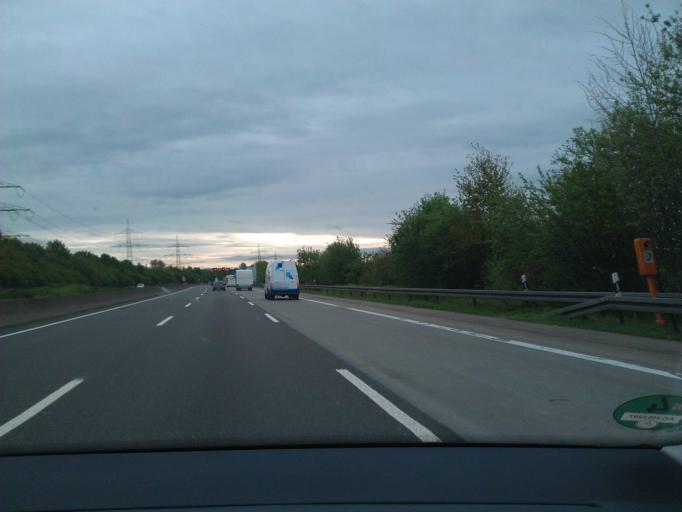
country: DE
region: North Rhine-Westphalia
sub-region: Regierungsbezirk Koln
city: Langerwehe
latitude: 50.8346
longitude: 6.3570
